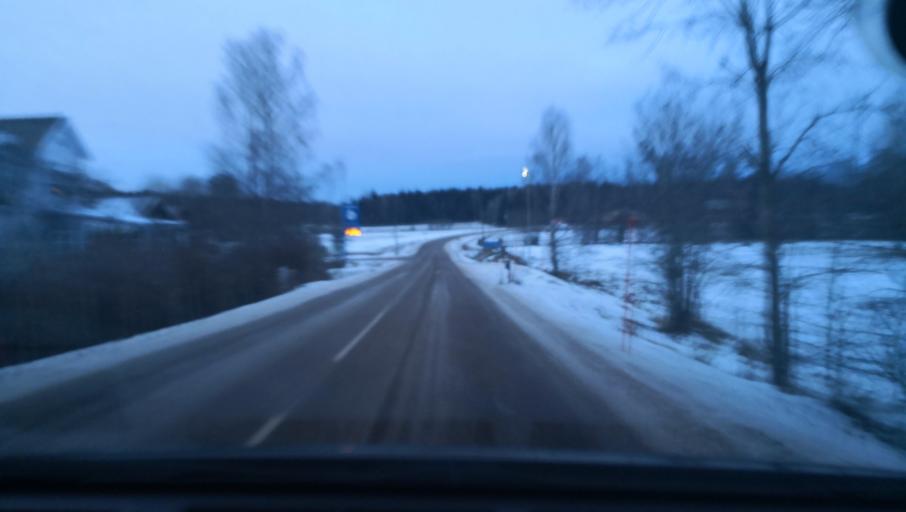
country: SE
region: Dalarna
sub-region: Avesta Kommun
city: Horndal
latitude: 60.1964
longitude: 16.4635
